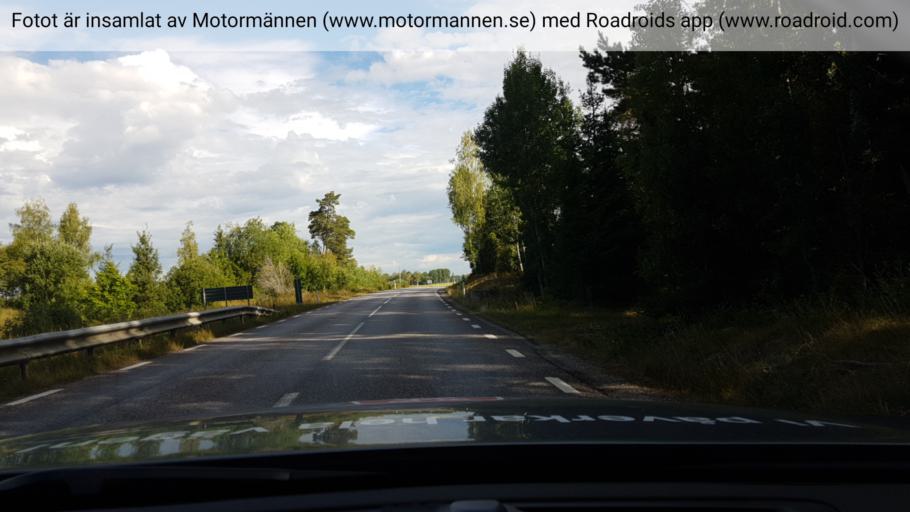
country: SE
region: Uppsala
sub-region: Enkopings Kommun
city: Irsta
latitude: 59.7777
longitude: 16.9072
